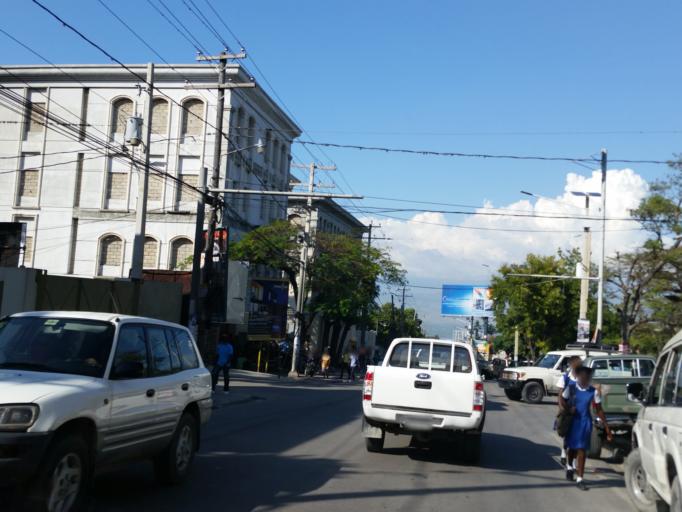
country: HT
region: Ouest
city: Petionville
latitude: 18.5122
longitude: -72.2830
